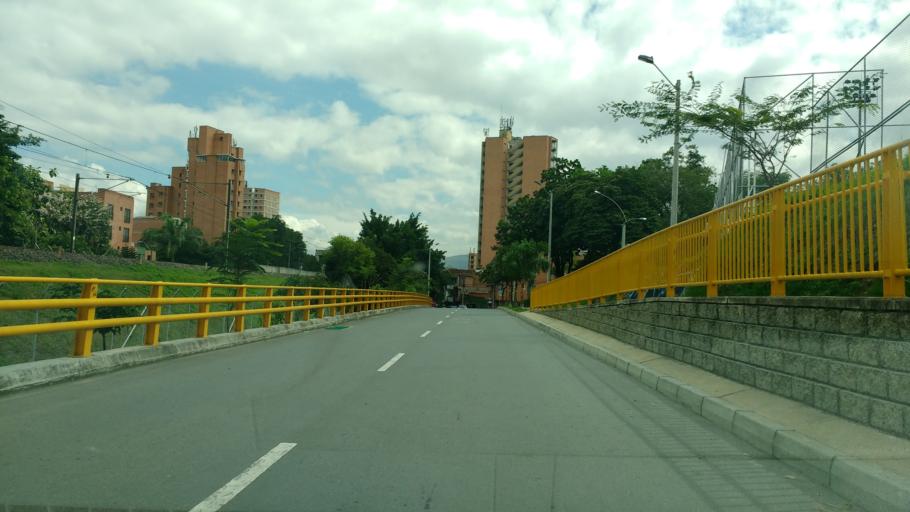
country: CO
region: Antioquia
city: Medellin
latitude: 6.2568
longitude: -75.6051
